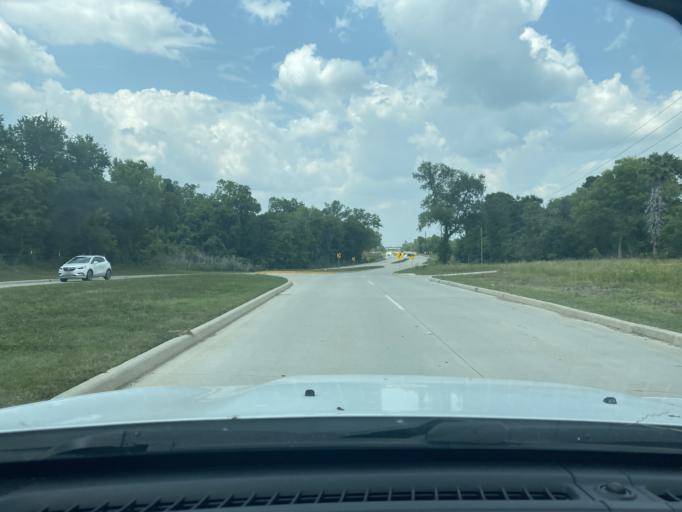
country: US
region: Texas
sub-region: Fort Bend County
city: Greatwood
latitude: 29.5434
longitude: -95.7235
